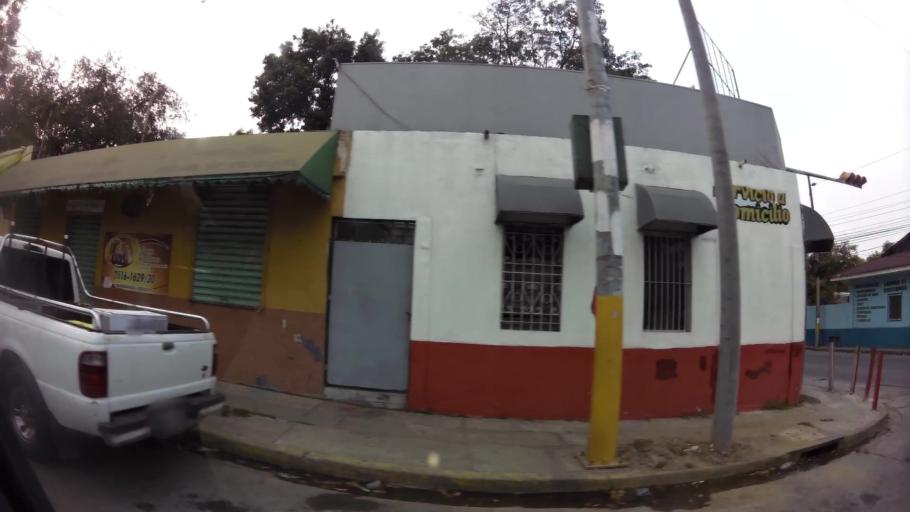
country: HN
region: Cortes
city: San Pedro Sula
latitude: 15.5115
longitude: -88.0280
